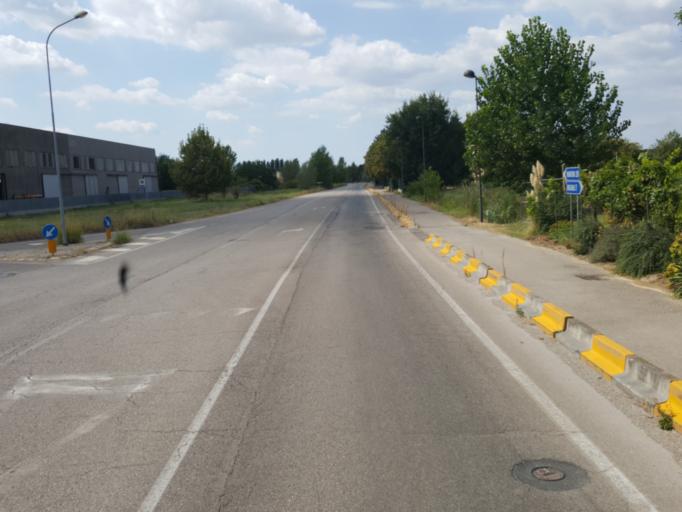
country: IT
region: Lombardy
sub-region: Provincia di Mantova
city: Villimpenta
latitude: 45.1447
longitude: 11.0098
